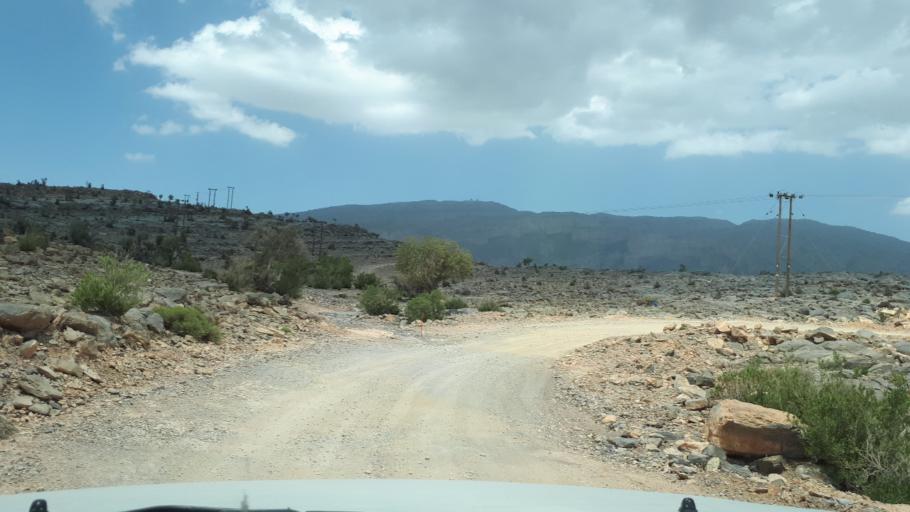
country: OM
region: Muhafazat ad Dakhiliyah
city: Bahla'
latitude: 23.2053
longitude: 57.2012
